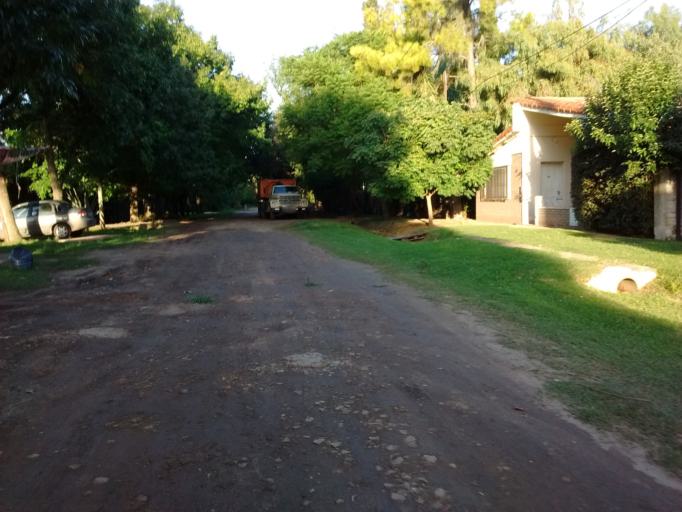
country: AR
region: Santa Fe
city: Funes
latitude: -32.9206
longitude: -60.8281
